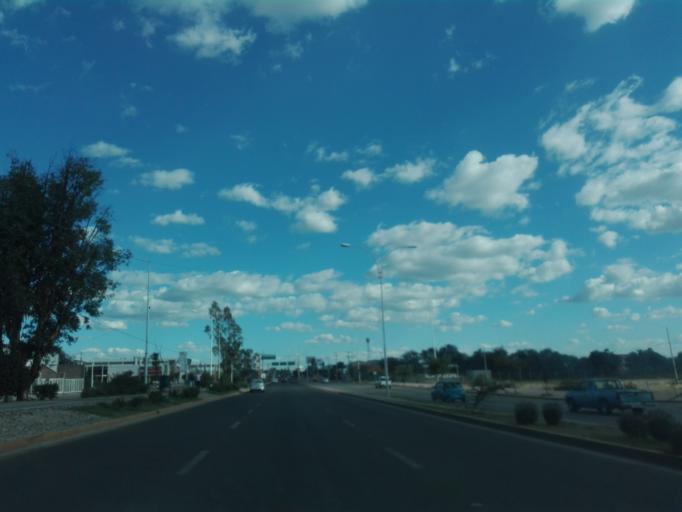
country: MX
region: Guanajuato
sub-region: Leon
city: Medina
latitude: 21.1670
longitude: -101.6530
